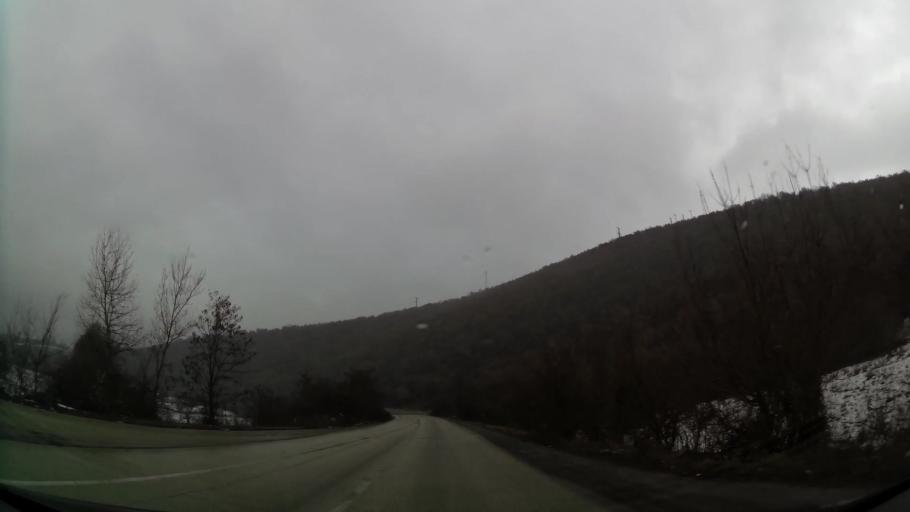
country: XK
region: Ferizaj
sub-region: Hani i Elezit
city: Hani i Elezit
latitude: 42.1297
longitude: 21.3124
